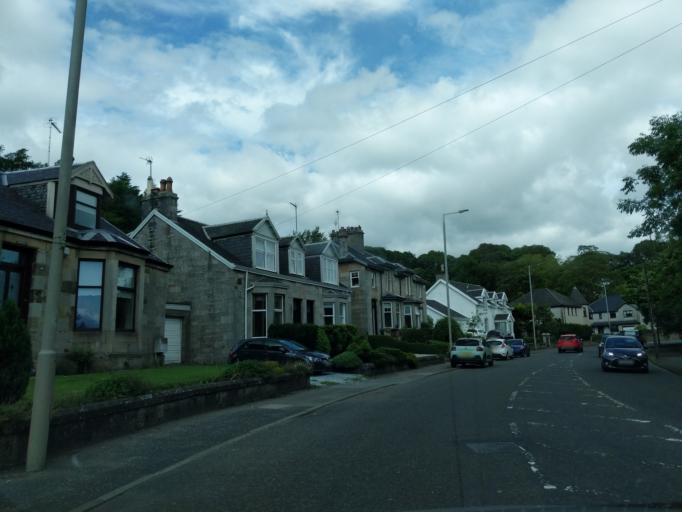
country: GB
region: Scotland
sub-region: South Lanarkshire
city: Strathaven
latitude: 55.6769
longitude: -4.0620
